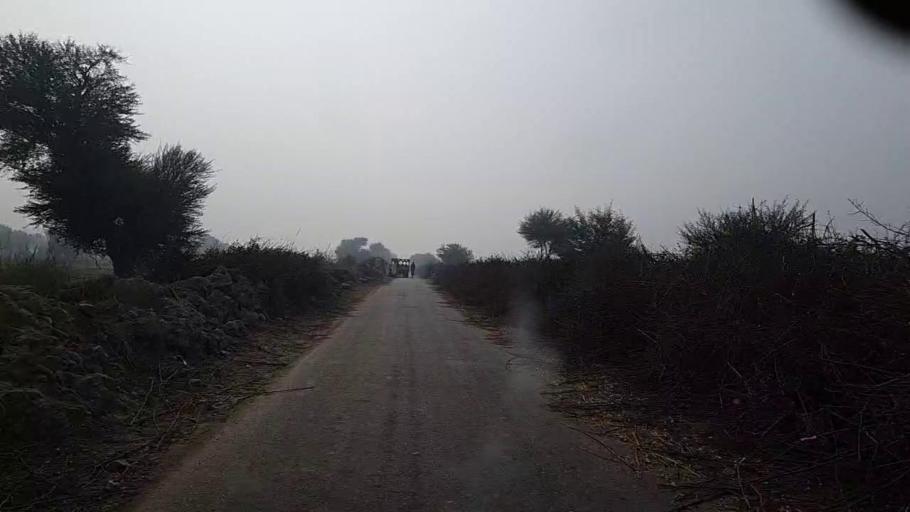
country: PK
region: Sindh
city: Kandiari
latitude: 26.9917
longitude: 68.6048
